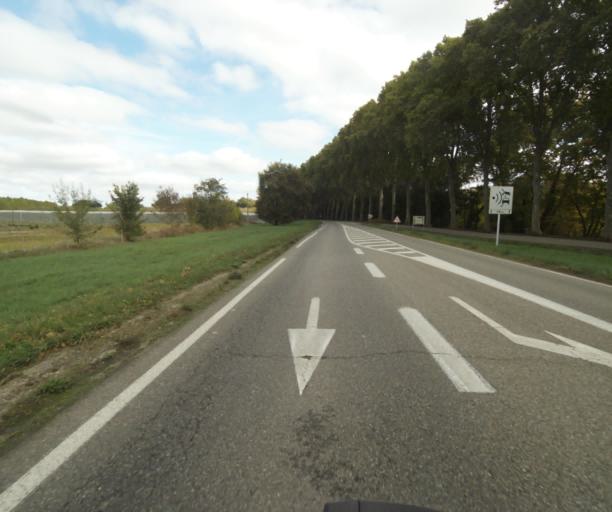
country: FR
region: Midi-Pyrenees
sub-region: Departement du Tarn-et-Garonne
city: Saint-Porquier
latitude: 43.9531
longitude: 1.1806
